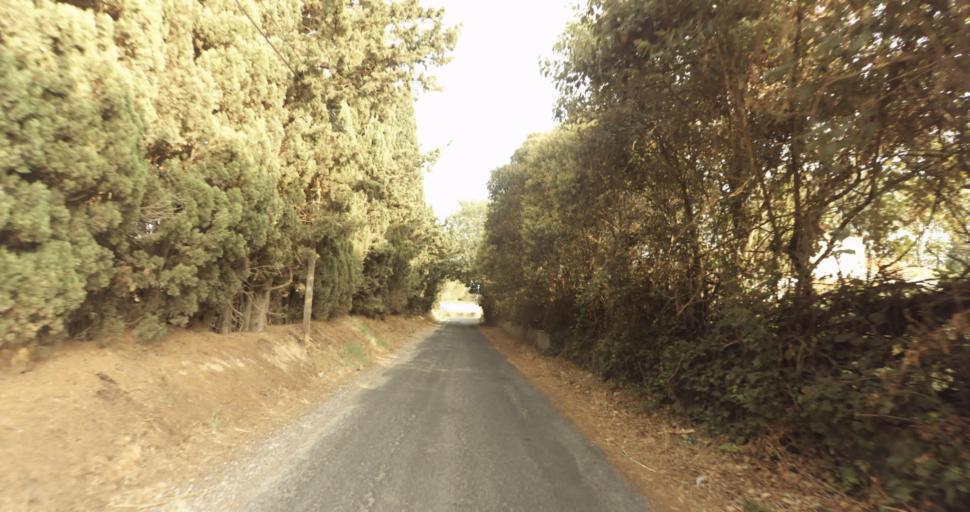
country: FR
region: Languedoc-Roussillon
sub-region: Departement des Pyrenees-Orientales
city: Theza
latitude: 42.6344
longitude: 2.9443
